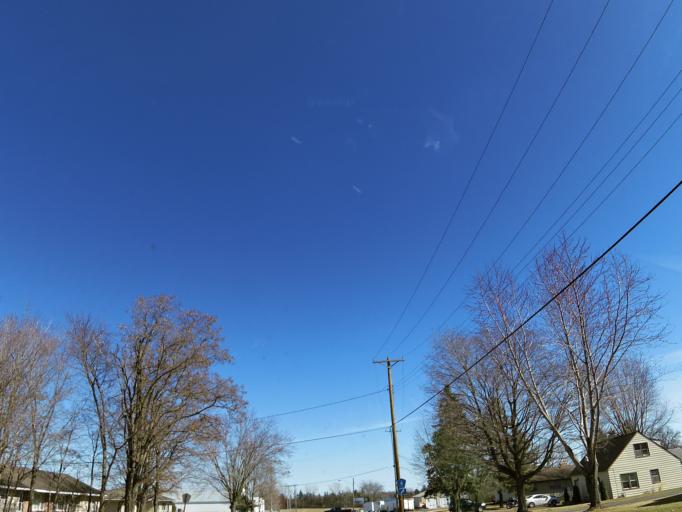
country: US
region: Minnesota
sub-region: Wright County
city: Maple Lake
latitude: 45.2295
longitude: -93.9957
